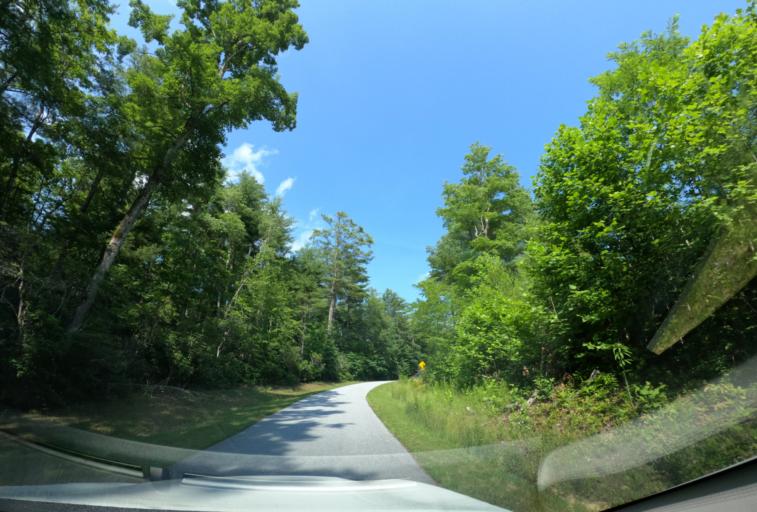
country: US
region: North Carolina
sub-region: Transylvania County
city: Brevard
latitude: 35.1017
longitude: -82.9458
